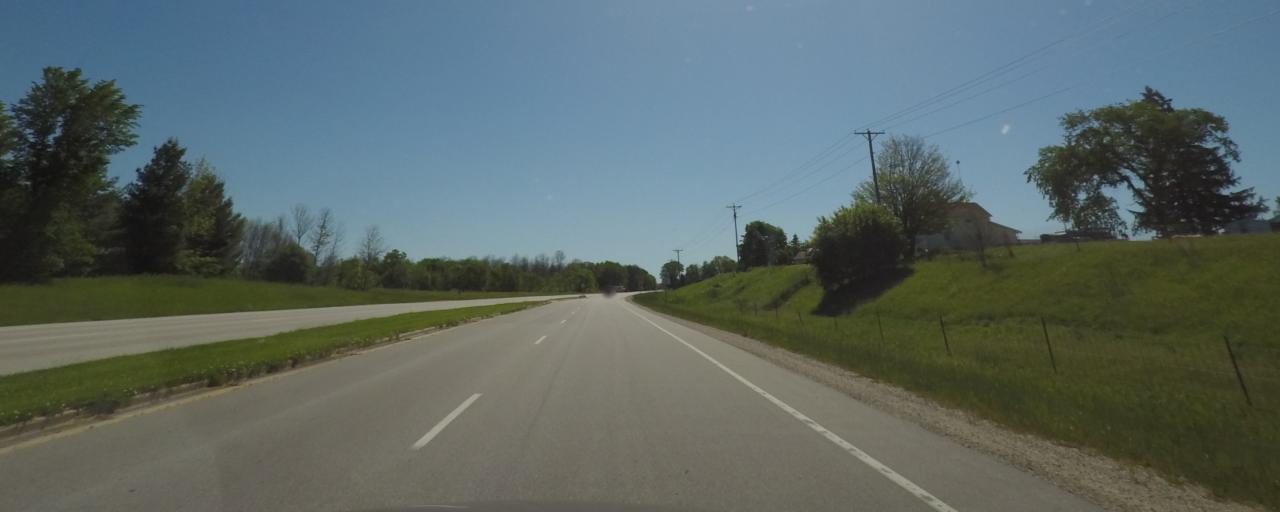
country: US
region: Wisconsin
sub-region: Sheboygan County
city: Plymouth
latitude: 43.7471
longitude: -87.9377
